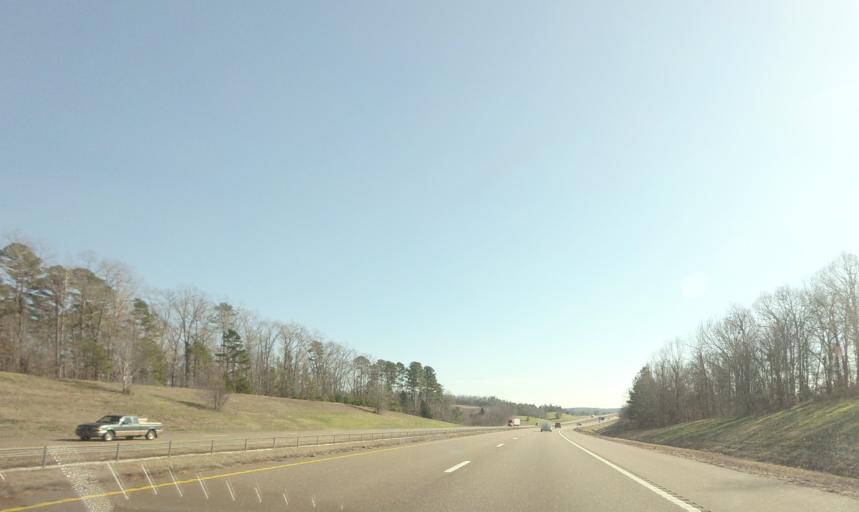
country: US
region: Mississippi
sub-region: Benton County
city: Ashland
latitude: 34.6273
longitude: -89.2087
